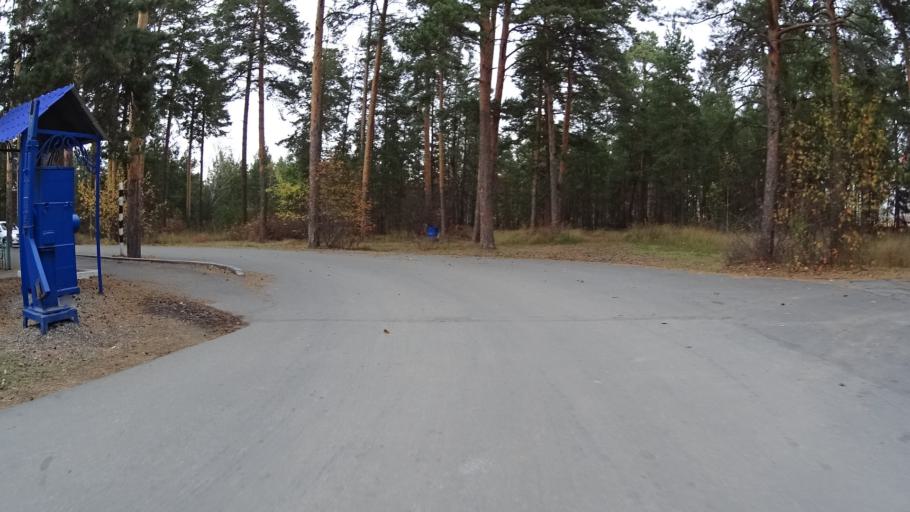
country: RU
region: Chelyabinsk
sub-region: Gorod Chelyabinsk
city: Chelyabinsk
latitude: 55.1681
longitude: 61.3638
